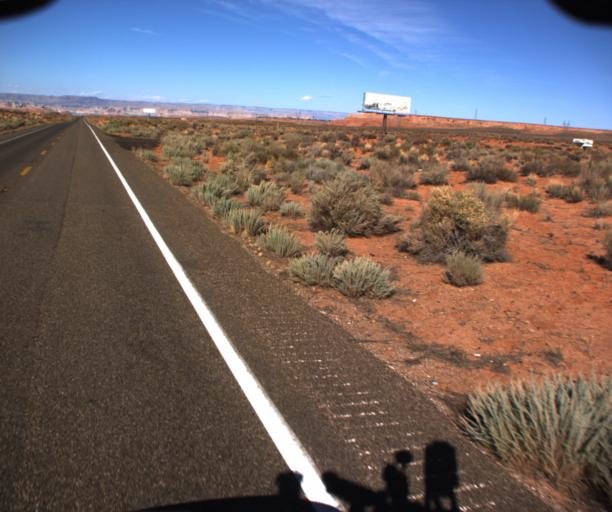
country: US
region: Arizona
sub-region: Coconino County
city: Page
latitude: 36.8655
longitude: -111.5040
